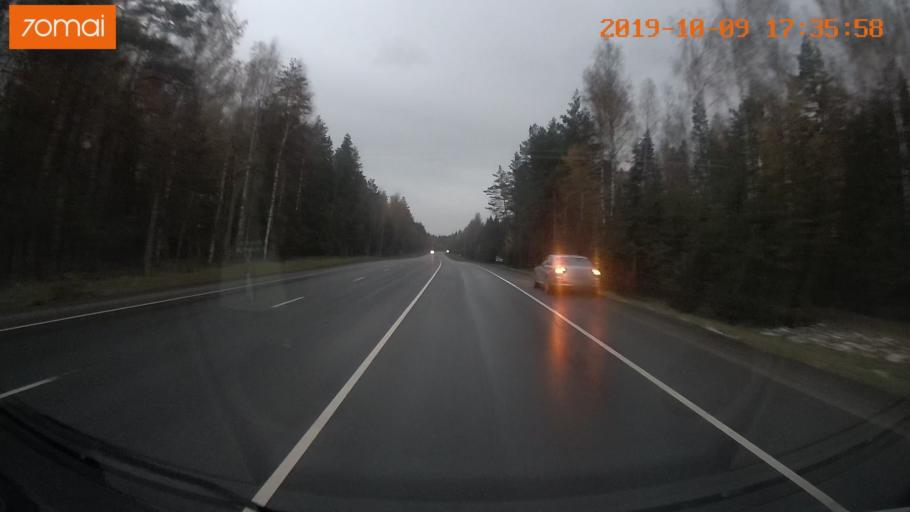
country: RU
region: Ivanovo
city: Bogorodskoye
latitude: 57.0856
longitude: 40.9987
